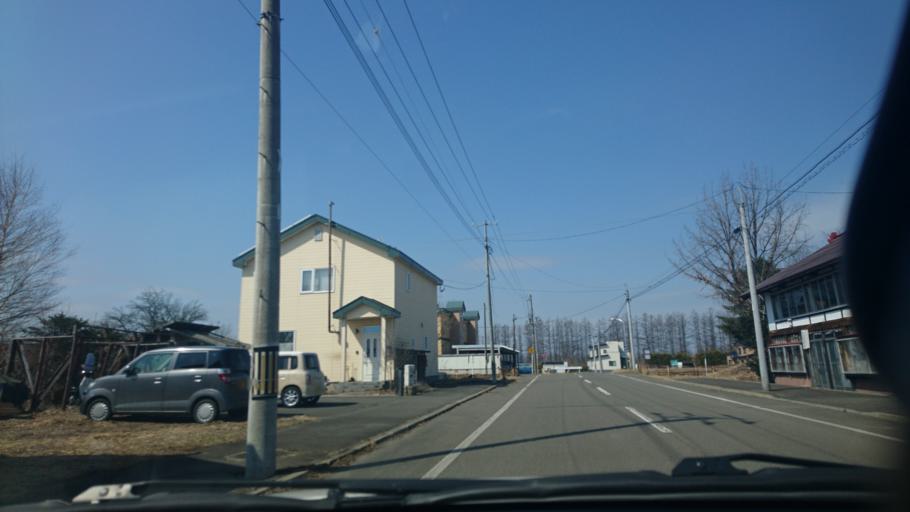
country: JP
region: Hokkaido
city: Otofuke
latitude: 43.0962
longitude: 143.2273
